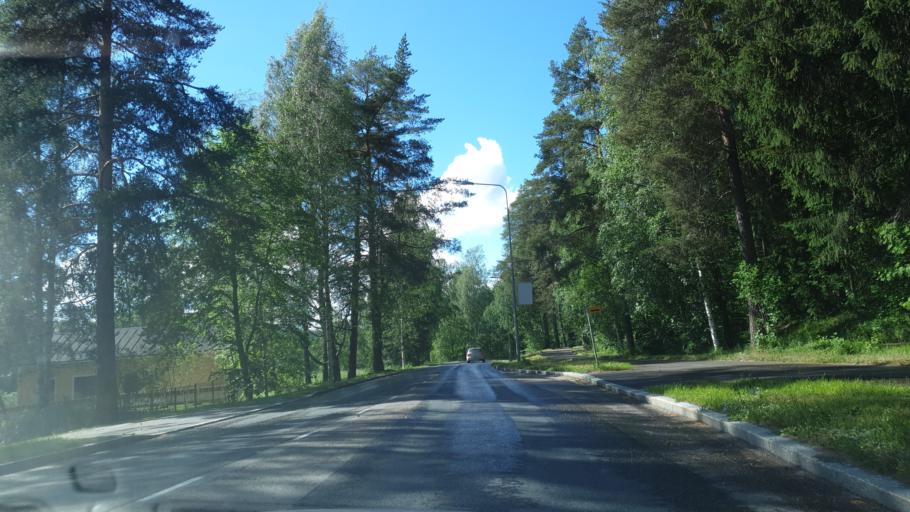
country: FI
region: Northern Savo
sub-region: Kuopio
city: Kuopio
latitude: 62.9158
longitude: 27.6339
